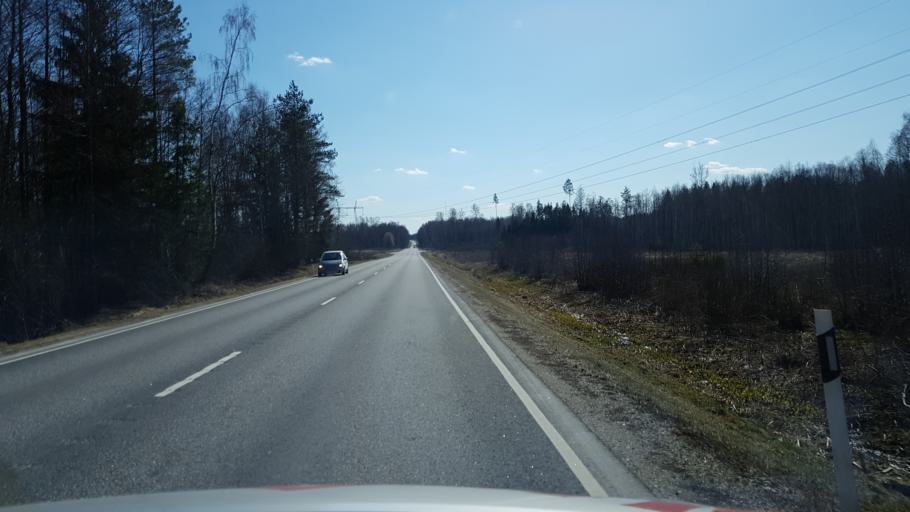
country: EE
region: Jogevamaa
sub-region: Mustvee linn
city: Mustvee
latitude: 58.6862
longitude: 26.8062
